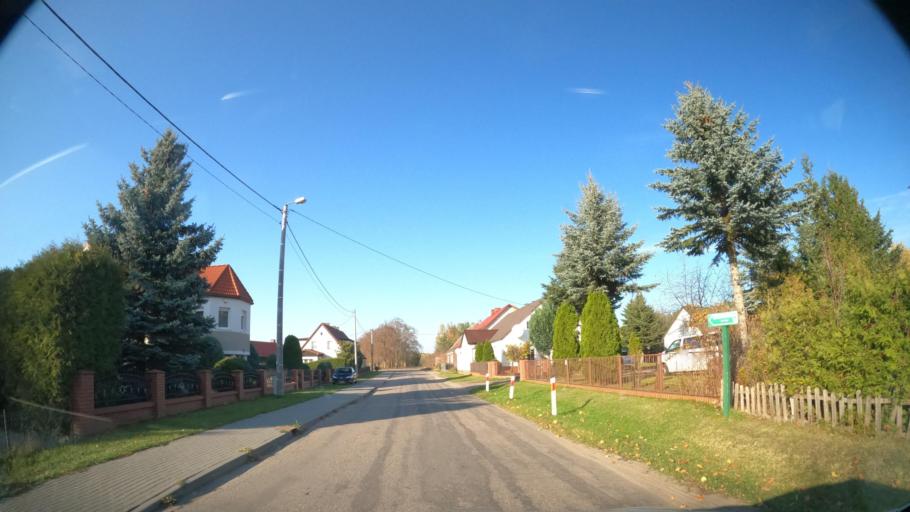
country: PL
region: Greater Poland Voivodeship
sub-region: Powiat zlotowski
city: Sypniewo
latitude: 53.3528
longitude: 16.5726
